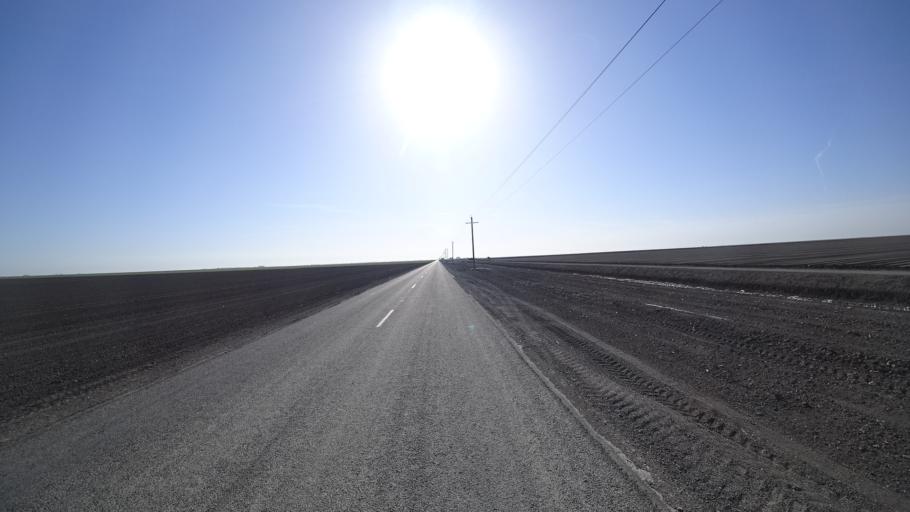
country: US
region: California
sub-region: Kings County
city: Corcoran
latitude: 36.0797
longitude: -119.7013
